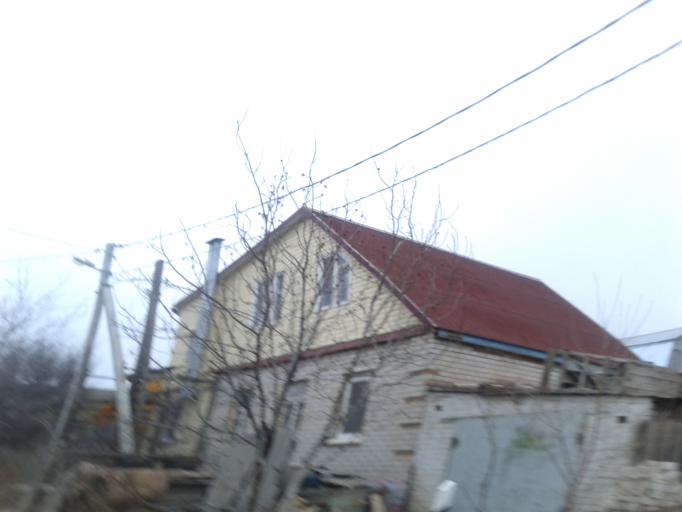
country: RU
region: Volgograd
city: Volgograd
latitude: 48.6545
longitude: 44.4175
